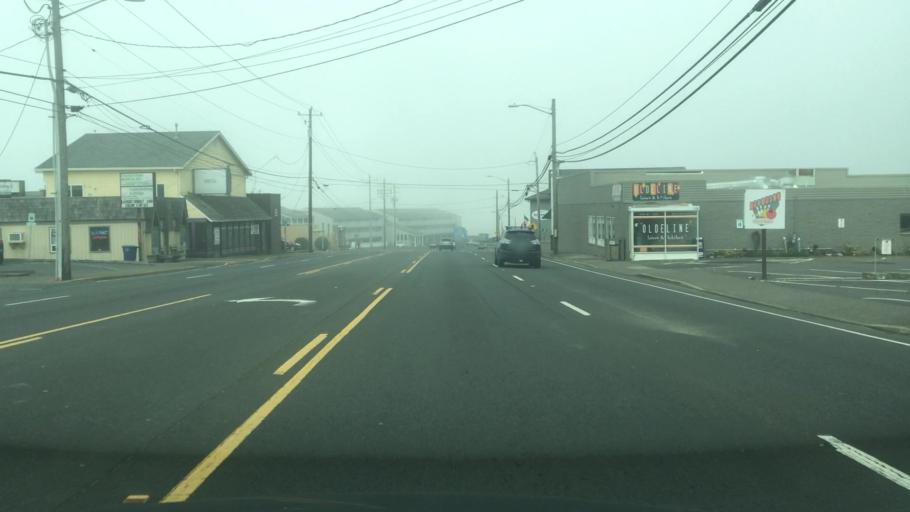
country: US
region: Oregon
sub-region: Lincoln County
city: Lincoln City
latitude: 44.9641
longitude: -124.0176
